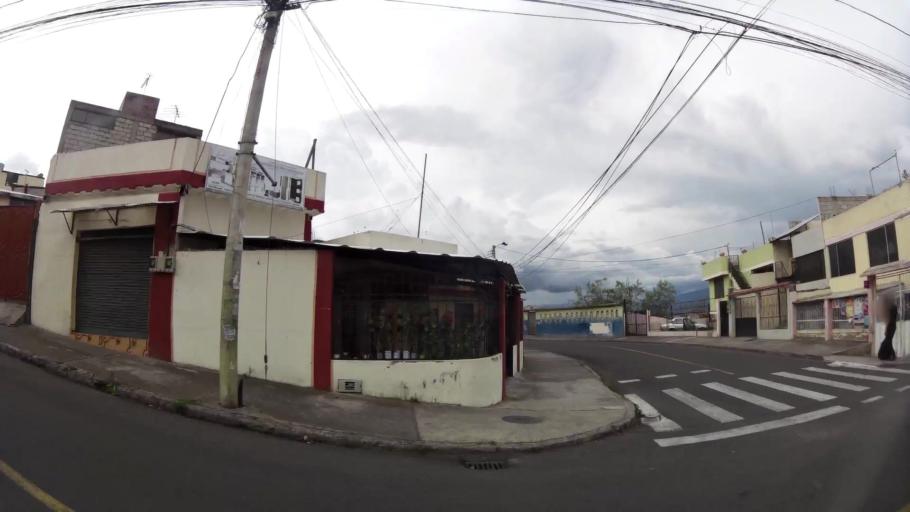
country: EC
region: Tungurahua
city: Ambato
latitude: -1.2628
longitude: -78.6320
